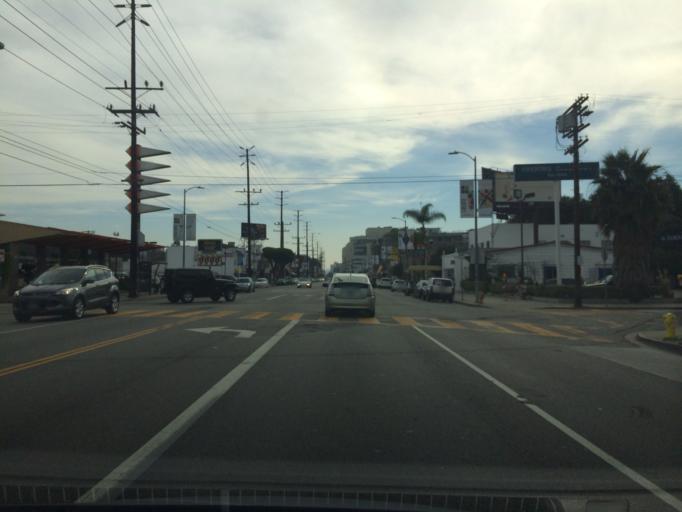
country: US
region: California
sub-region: Los Angeles County
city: West Hollywood
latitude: 34.0805
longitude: -118.3766
